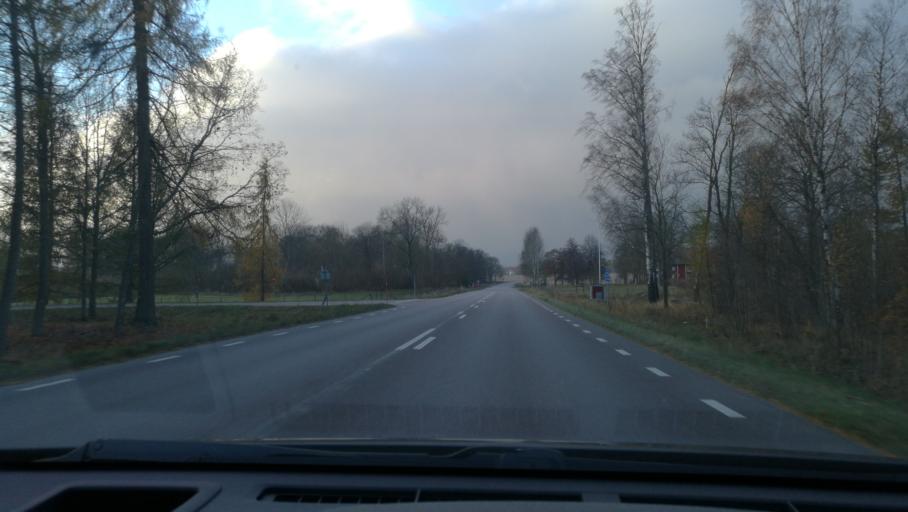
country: SE
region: Soedermanland
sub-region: Vingakers Kommun
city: Vingaker
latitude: 59.1507
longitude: 16.0463
